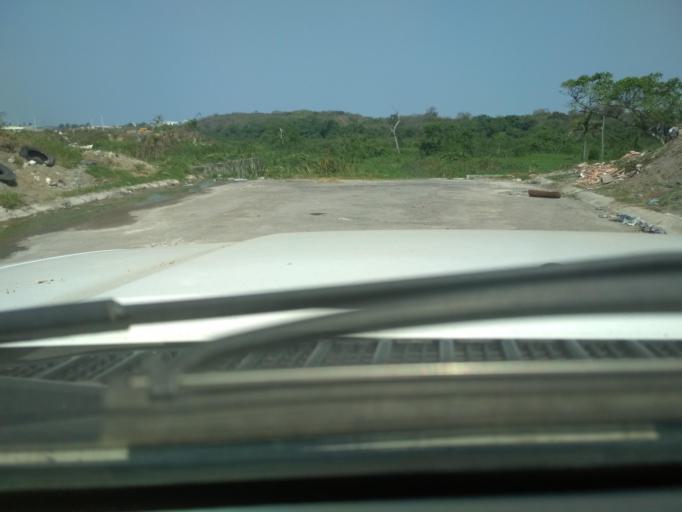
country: MX
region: Veracruz
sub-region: Veracruz
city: Lomas de Rio Medio Cuatro
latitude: 19.1884
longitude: -96.2057
